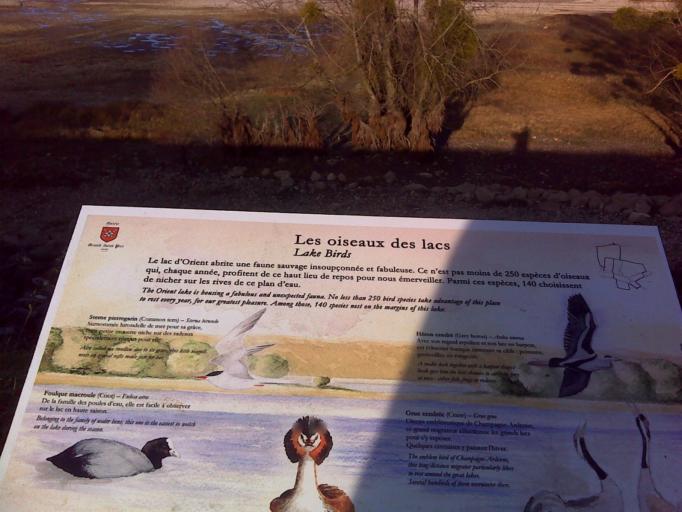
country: FR
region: Champagne-Ardenne
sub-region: Departement de l'Aube
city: Lusigny-sur-Barse
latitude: 48.2531
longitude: 4.3326
